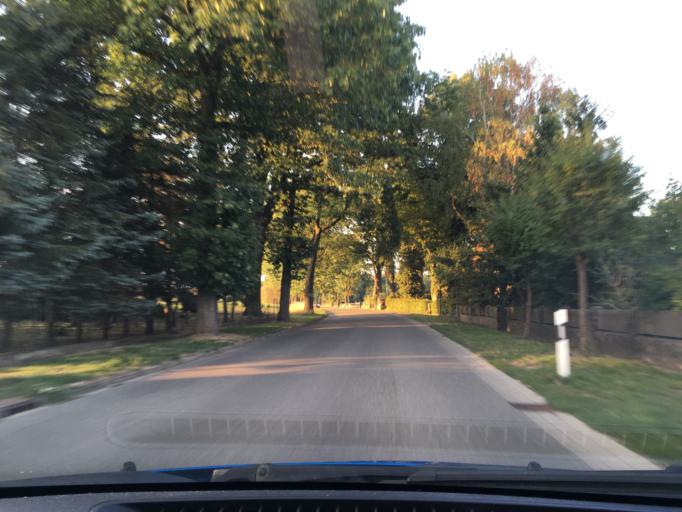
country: DE
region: Lower Saxony
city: Bleckede
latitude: 53.2626
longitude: 10.7432
